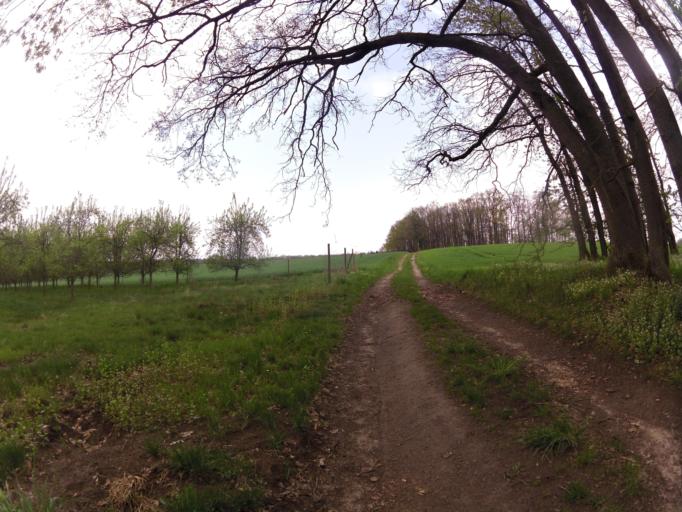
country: DE
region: Bavaria
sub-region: Regierungsbezirk Unterfranken
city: Sommerhausen
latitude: 49.7005
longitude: 10.0605
